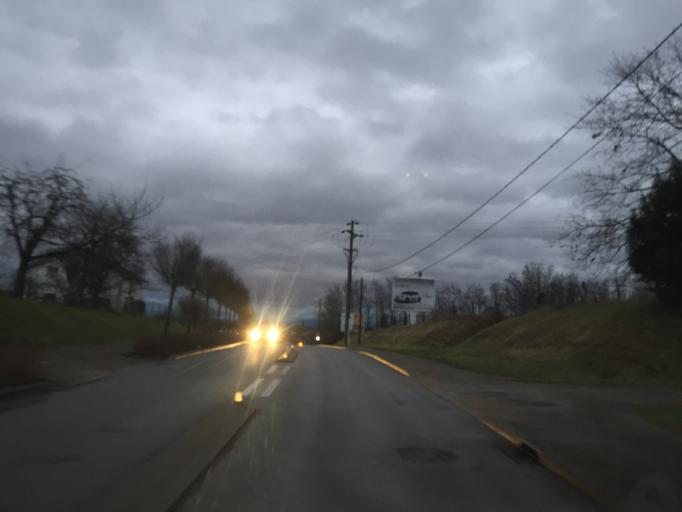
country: FR
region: Franche-Comte
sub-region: Departement du Jura
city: Dole
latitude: 47.1057
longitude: 5.4843
